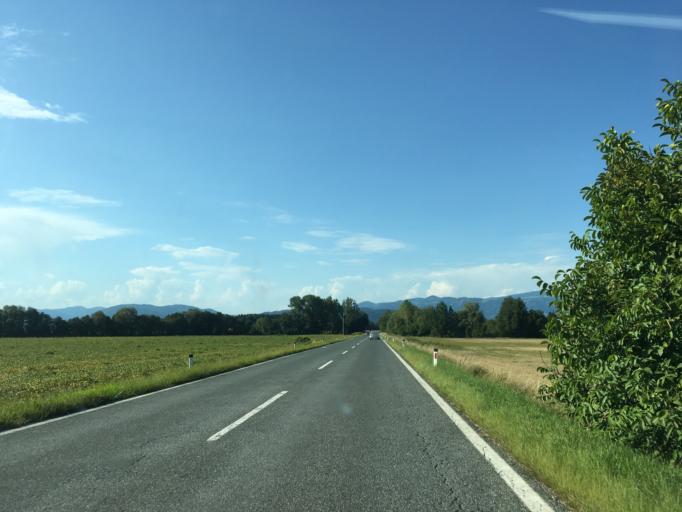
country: AT
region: Carinthia
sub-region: Politischer Bezirk Volkermarkt
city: Eberndorf
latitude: 46.5940
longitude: 14.6357
